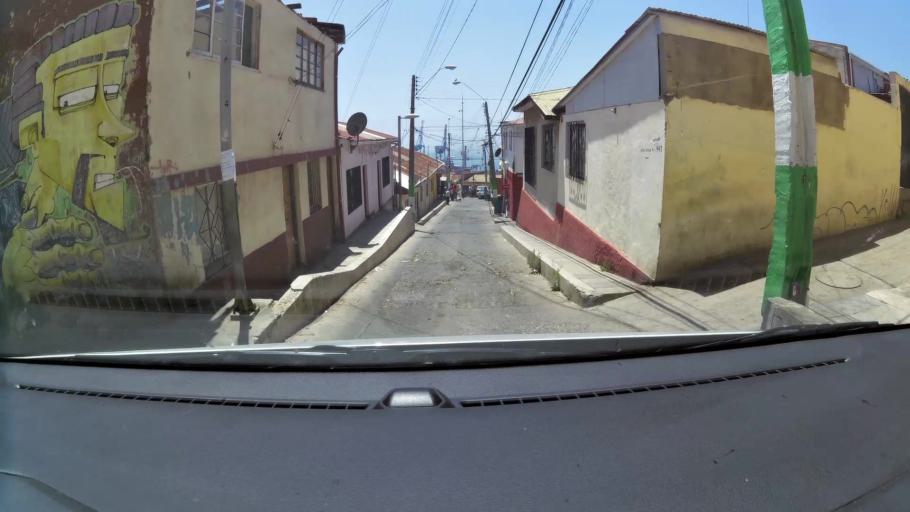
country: CL
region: Valparaiso
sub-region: Provincia de Valparaiso
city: Valparaiso
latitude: -33.0376
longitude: -71.6358
